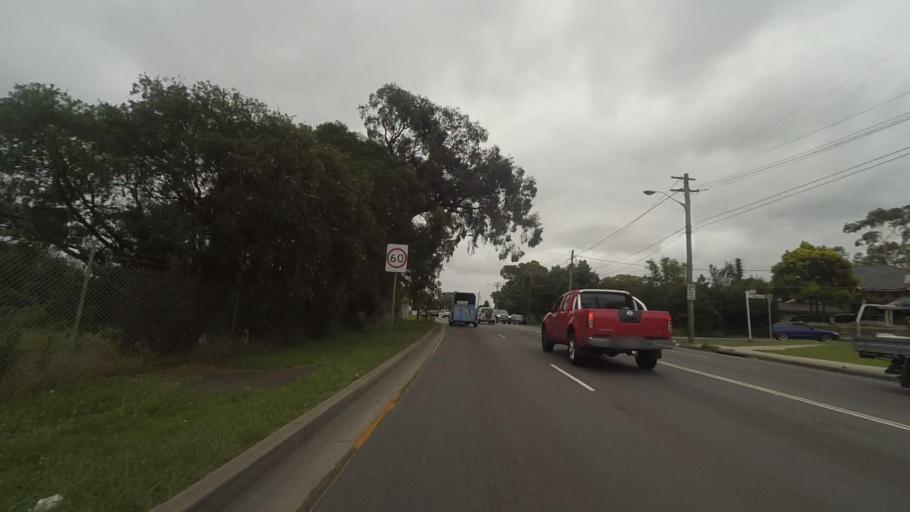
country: AU
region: New South Wales
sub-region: Bankstown
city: Bankstown
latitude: -33.9088
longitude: 151.0412
